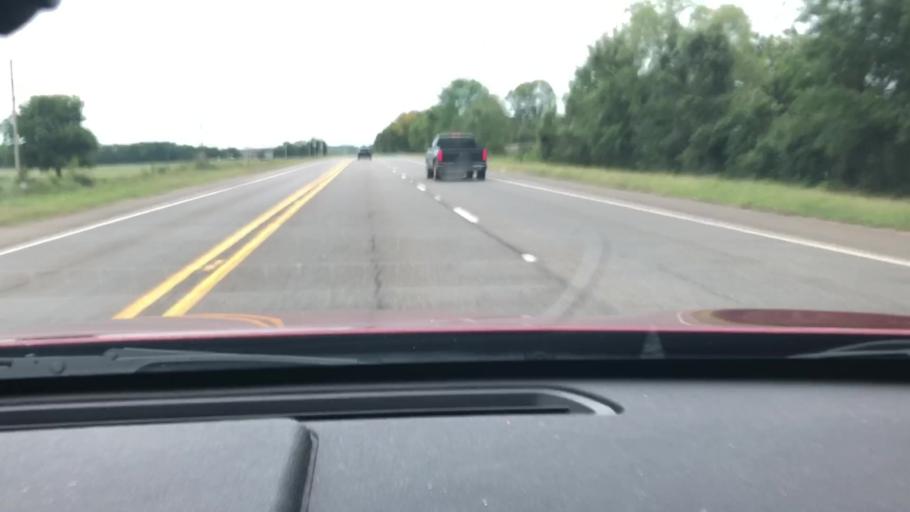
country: US
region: Arkansas
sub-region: Lafayette County
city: Lewisville
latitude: 33.3558
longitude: -93.6588
